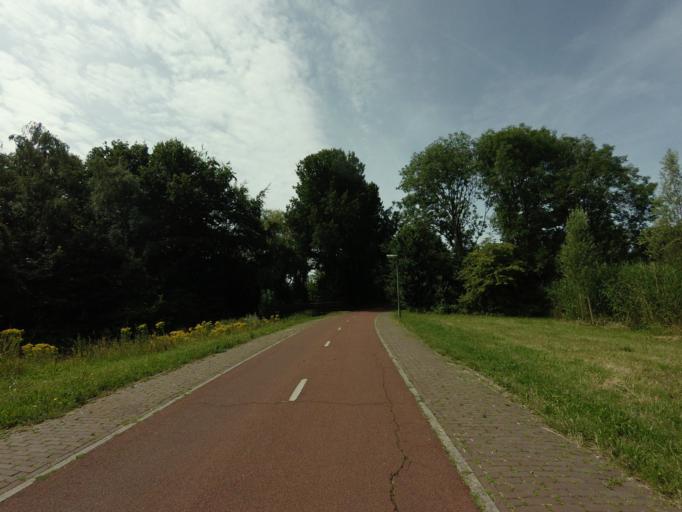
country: NL
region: South Holland
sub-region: Gemeente Westland
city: Kwintsheul
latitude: 52.0559
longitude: 4.2589
